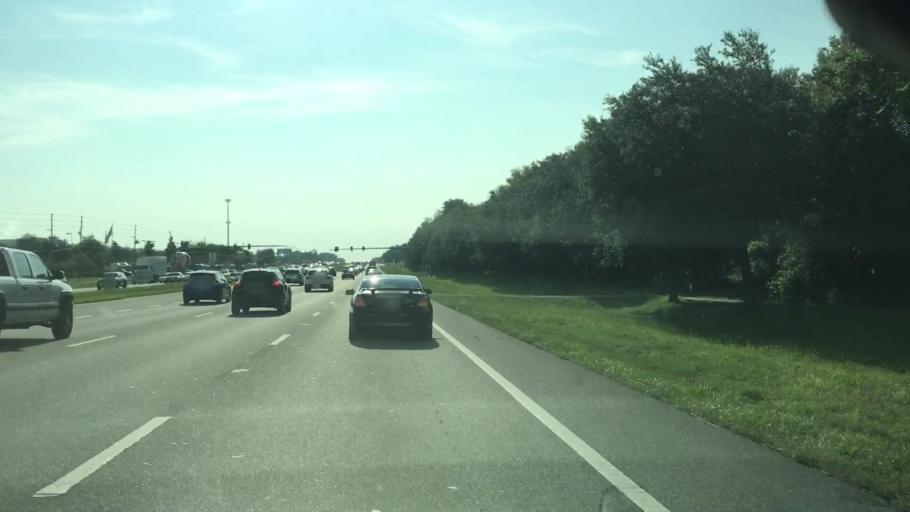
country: US
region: Florida
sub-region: Pasco County
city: Land O' Lakes
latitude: 28.1863
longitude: -82.4117
